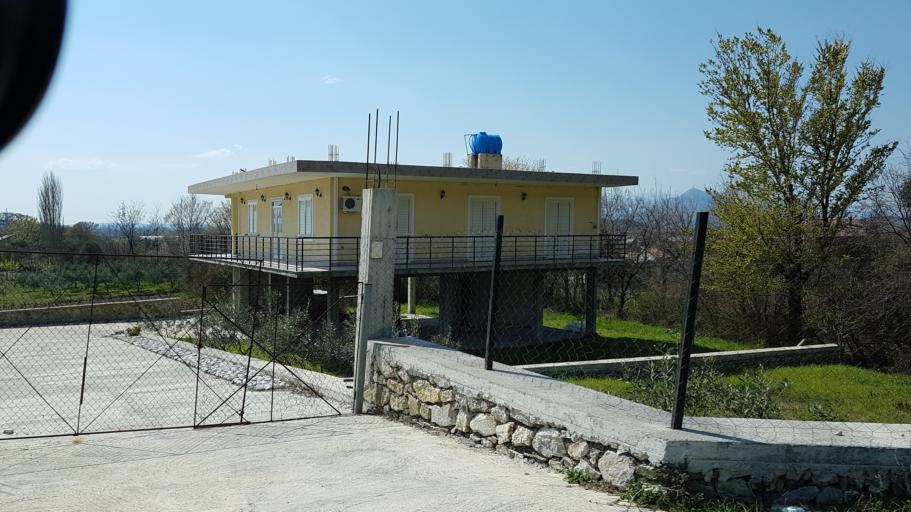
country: AL
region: Shkoder
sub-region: Rrethi i Shkodres
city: Guri i Zi
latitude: 42.0179
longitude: 19.5791
